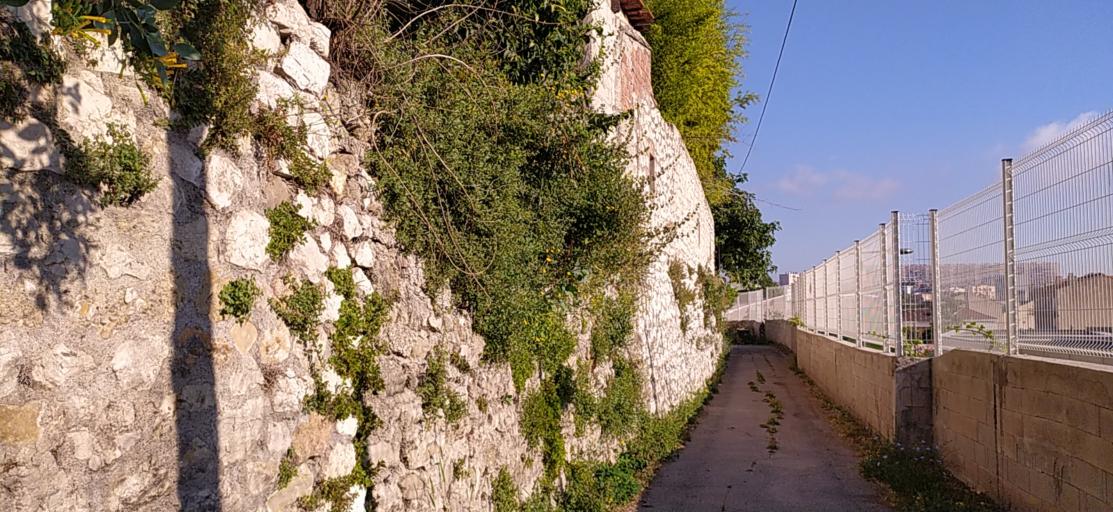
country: FR
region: Provence-Alpes-Cote d'Azur
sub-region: Departement des Bouches-du-Rhone
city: Marseille 14
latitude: 43.3315
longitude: 5.3587
